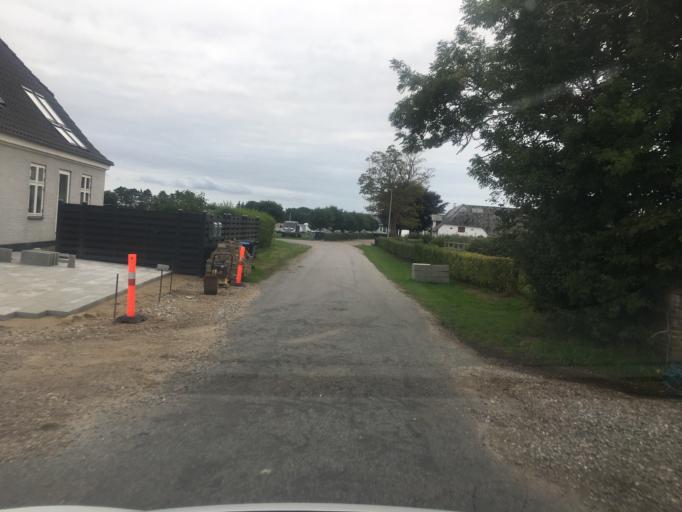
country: DK
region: South Denmark
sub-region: Tonder Kommune
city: Tonder
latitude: 54.9589
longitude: 8.9222
